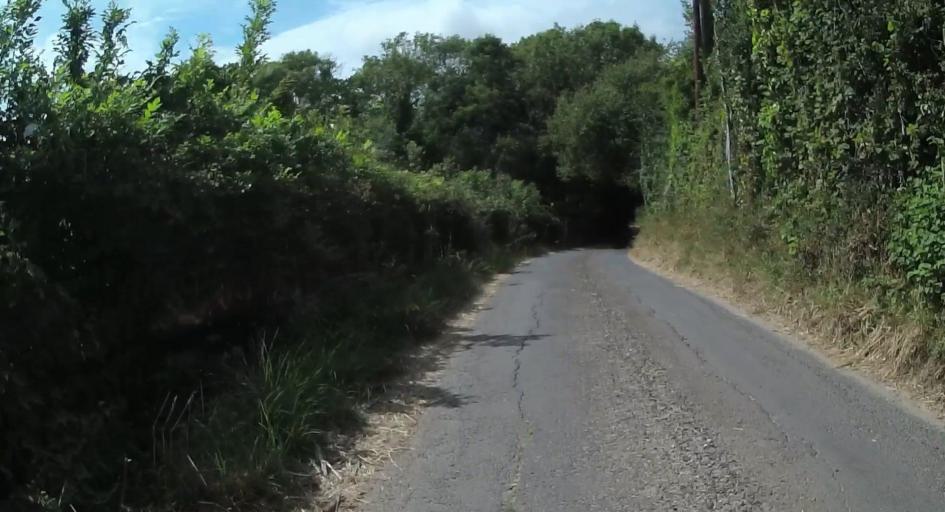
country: GB
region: England
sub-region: Dorset
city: Swanage
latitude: 50.6311
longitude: -2.0138
